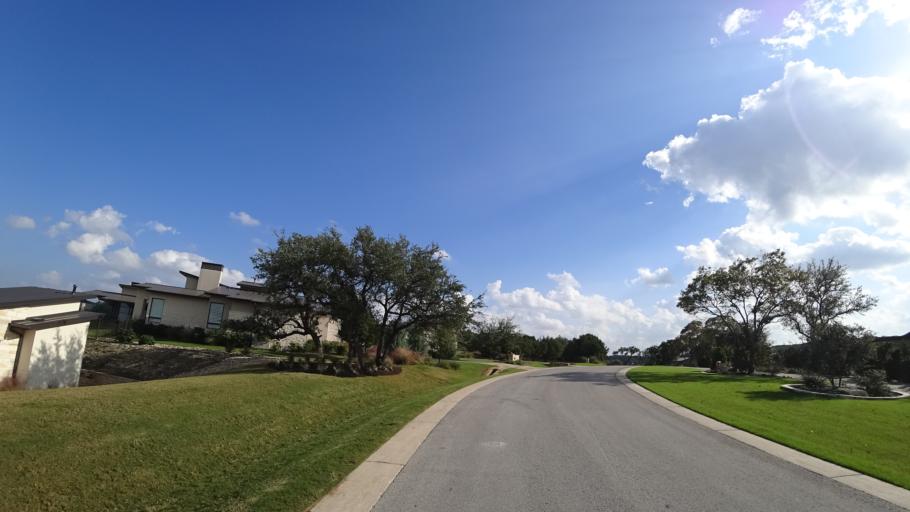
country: US
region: Texas
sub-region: Travis County
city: Barton Creek
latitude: 30.2711
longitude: -97.8815
